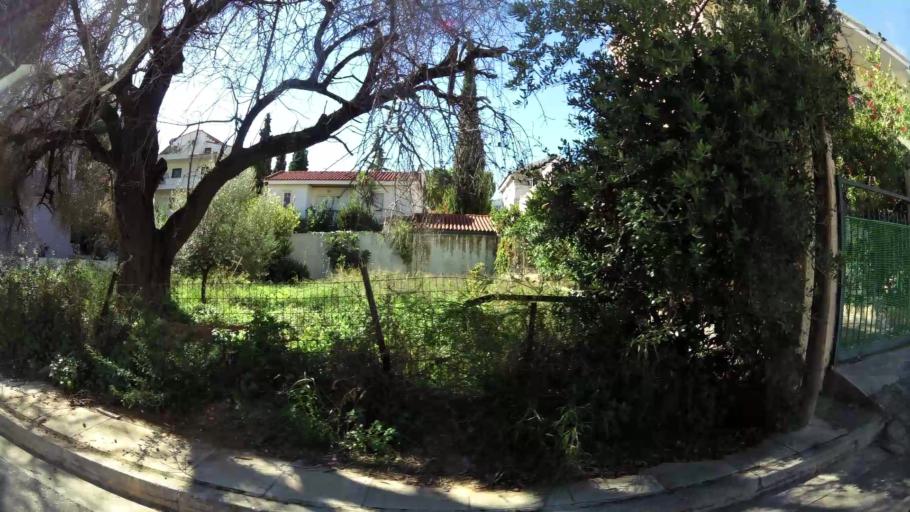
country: GR
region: Attica
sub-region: Nomarchia Anatolikis Attikis
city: Leondarion
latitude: 37.9808
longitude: 23.8590
